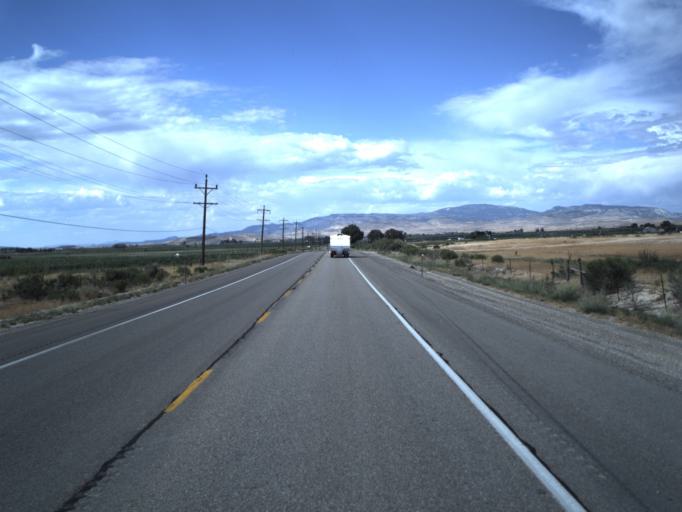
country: US
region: Utah
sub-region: Sanpete County
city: Centerfield
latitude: 39.0631
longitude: -111.8208
